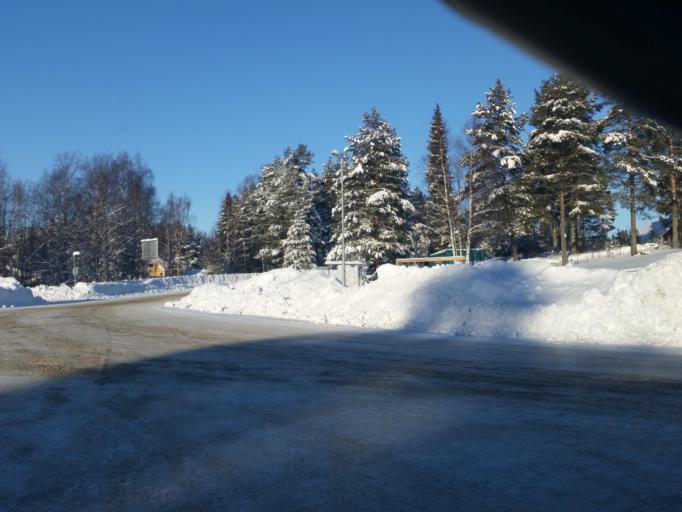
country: SE
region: Norrbotten
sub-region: Pitea Kommun
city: Pitea
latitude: 65.1435
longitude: 21.5030
